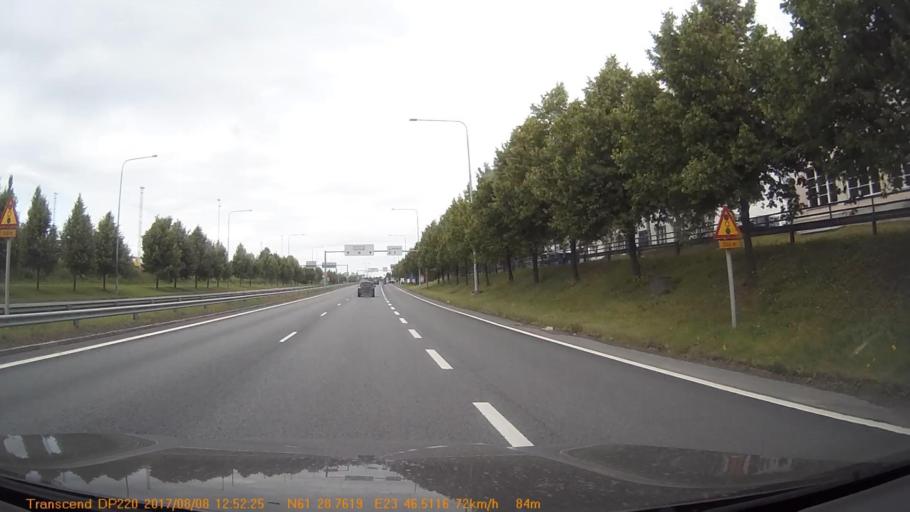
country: FI
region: Pirkanmaa
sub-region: Tampere
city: Tampere
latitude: 61.4795
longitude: 23.7753
